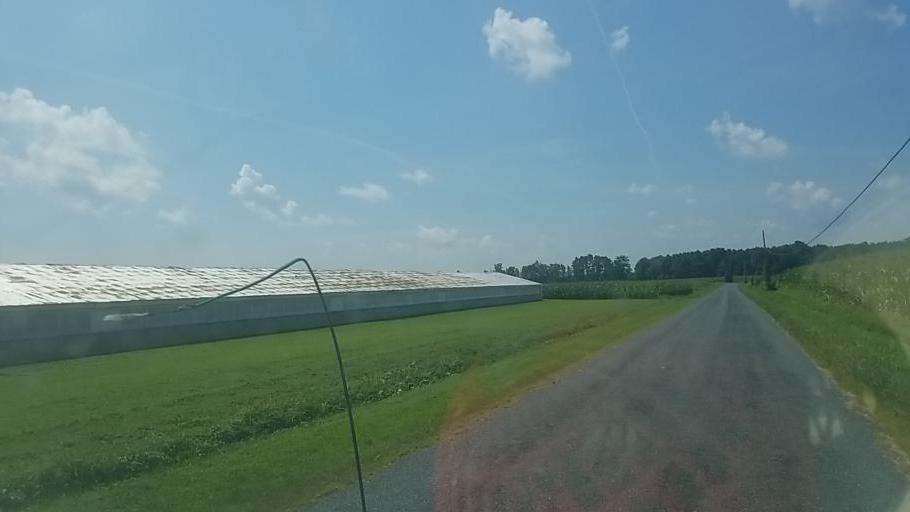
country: US
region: Maryland
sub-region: Worcester County
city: Berlin
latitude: 38.2948
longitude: -75.2936
